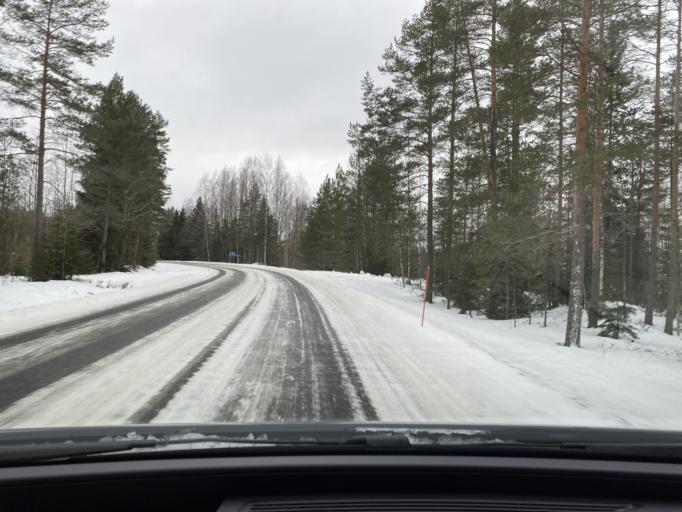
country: FI
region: Pirkanmaa
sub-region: Lounais-Pirkanmaa
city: Punkalaidun
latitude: 61.1604
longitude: 23.0547
